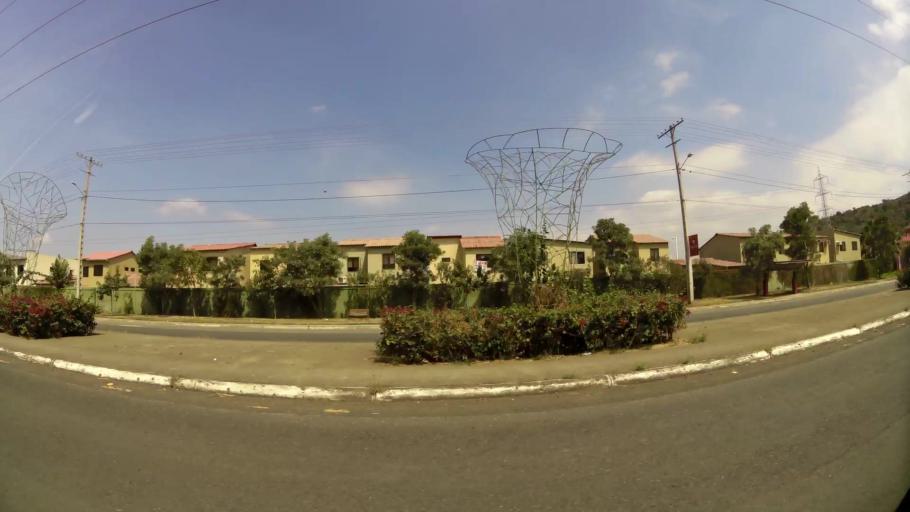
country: EC
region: Guayas
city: El Triunfo
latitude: -2.0341
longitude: -79.8974
